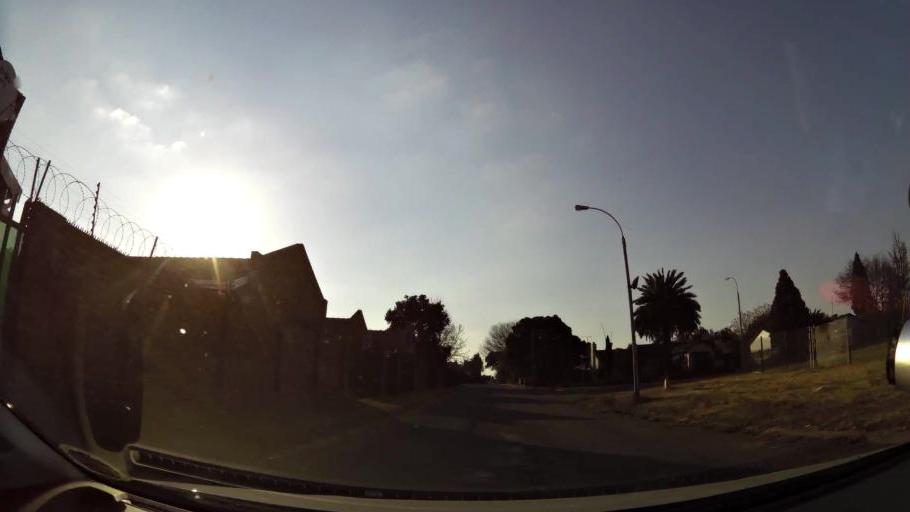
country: ZA
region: Gauteng
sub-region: City of Johannesburg Metropolitan Municipality
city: Modderfontein
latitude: -26.0694
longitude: 28.2200
